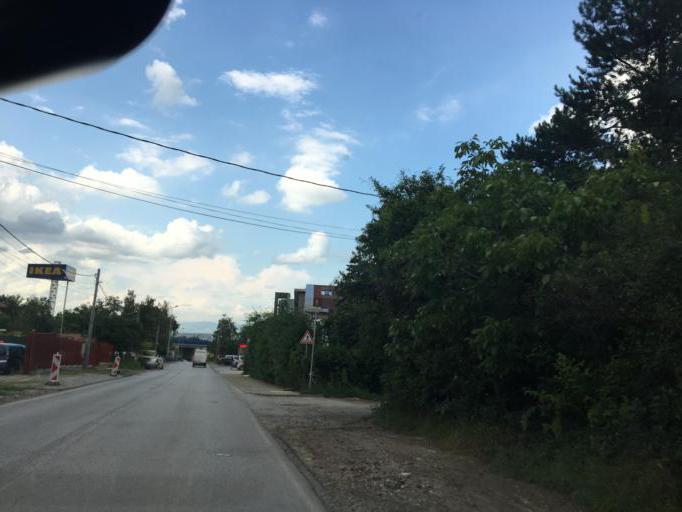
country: BG
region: Sofia-Capital
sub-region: Stolichna Obshtina
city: Sofia
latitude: 42.6213
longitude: 23.3587
